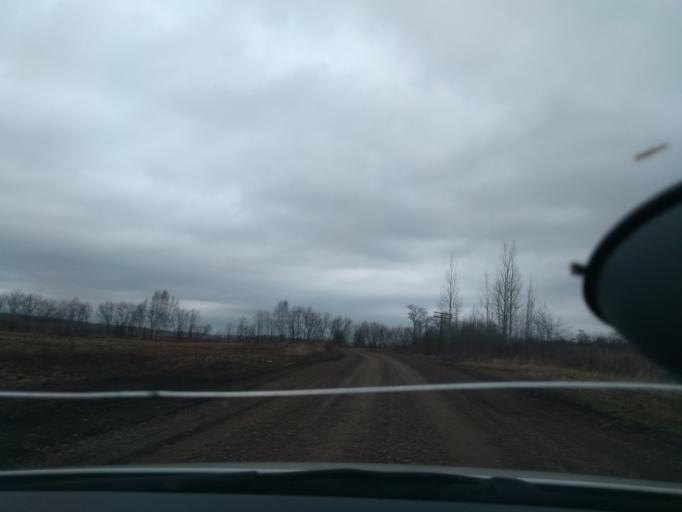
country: RU
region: Perm
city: Orda
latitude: 57.2459
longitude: 56.6112
